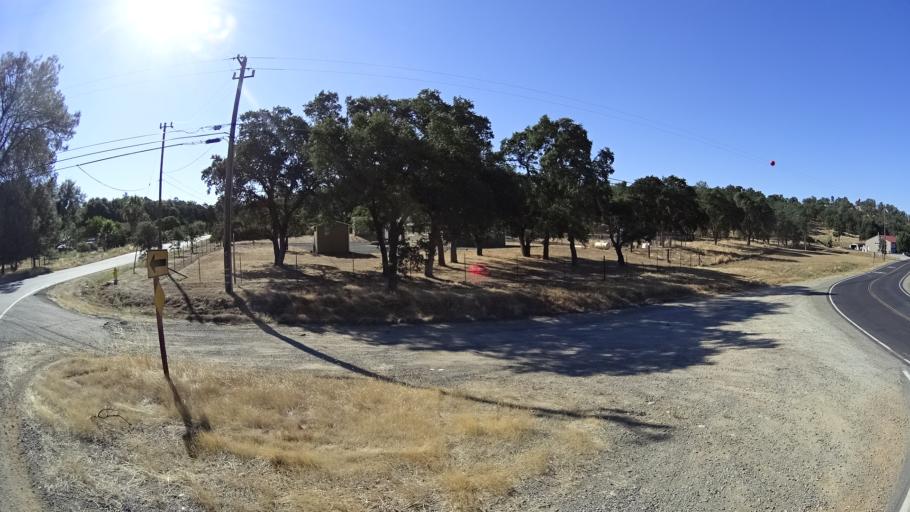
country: US
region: California
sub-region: Calaveras County
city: Rancho Calaveras
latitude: 38.1222
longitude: -120.8770
